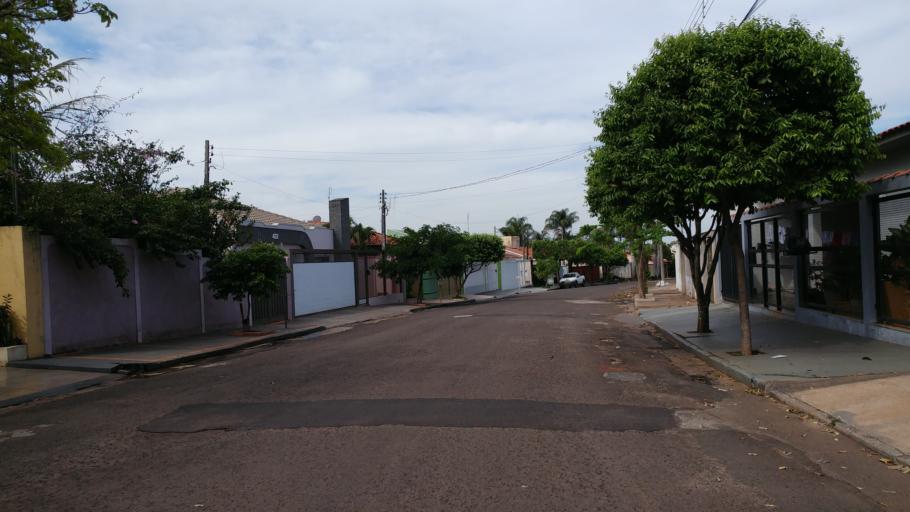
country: BR
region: Sao Paulo
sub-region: Paraguacu Paulista
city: Paraguacu Paulista
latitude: -22.4052
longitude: -50.5793
